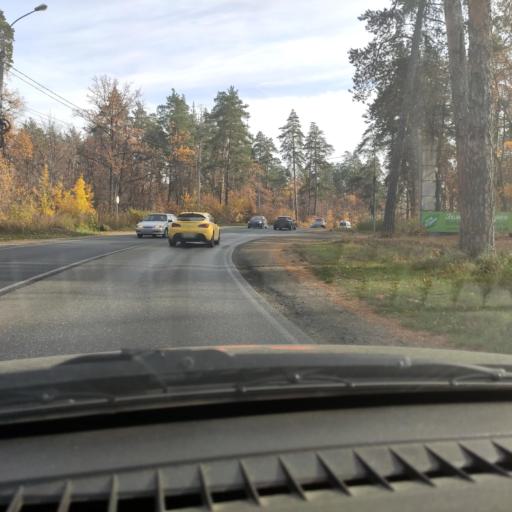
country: RU
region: Samara
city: Tol'yatti
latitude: 53.4916
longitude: 49.3050
